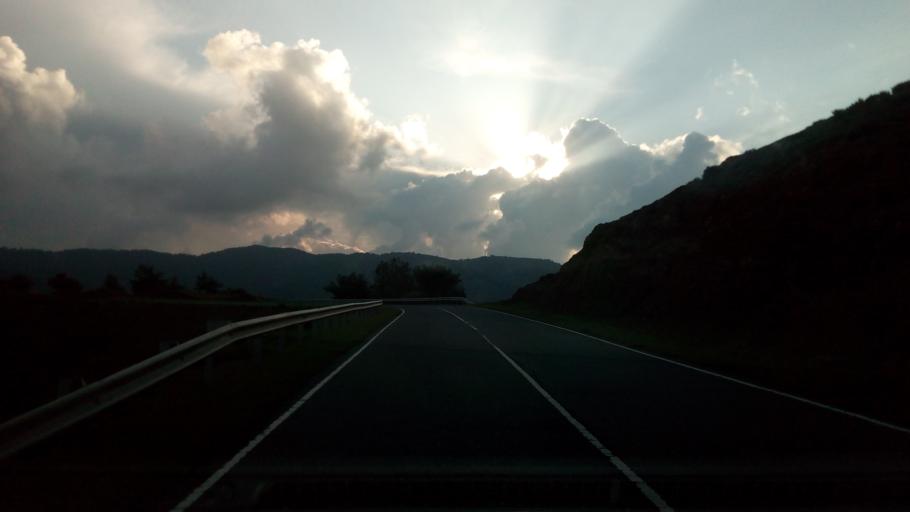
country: CY
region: Lefkosia
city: Kato Pyrgos
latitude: 35.1650
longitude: 32.6233
